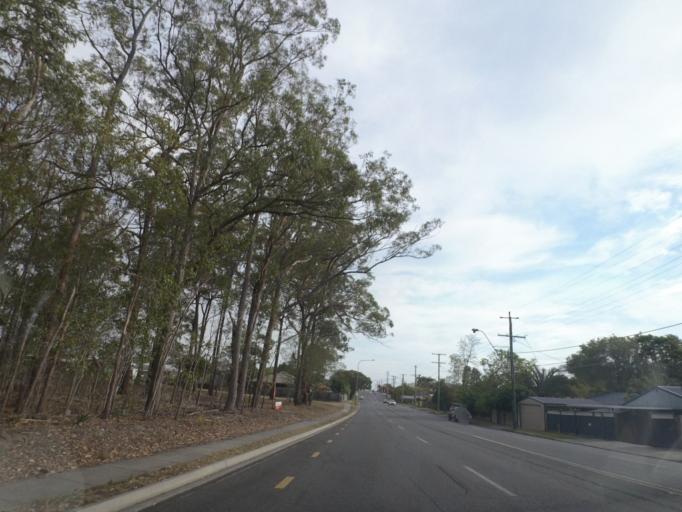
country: AU
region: Queensland
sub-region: Brisbane
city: Coopers Plains
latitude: -27.5520
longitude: 153.0418
